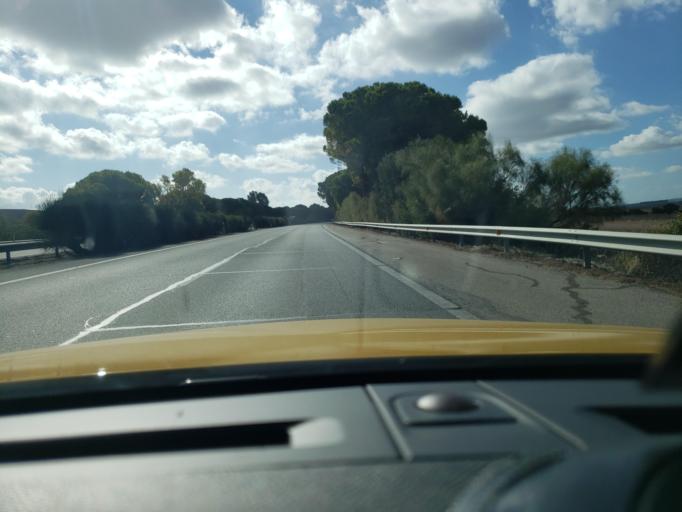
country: ES
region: Andalusia
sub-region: Provincia de Sevilla
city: Lebrija
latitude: 36.8600
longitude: -5.9953
